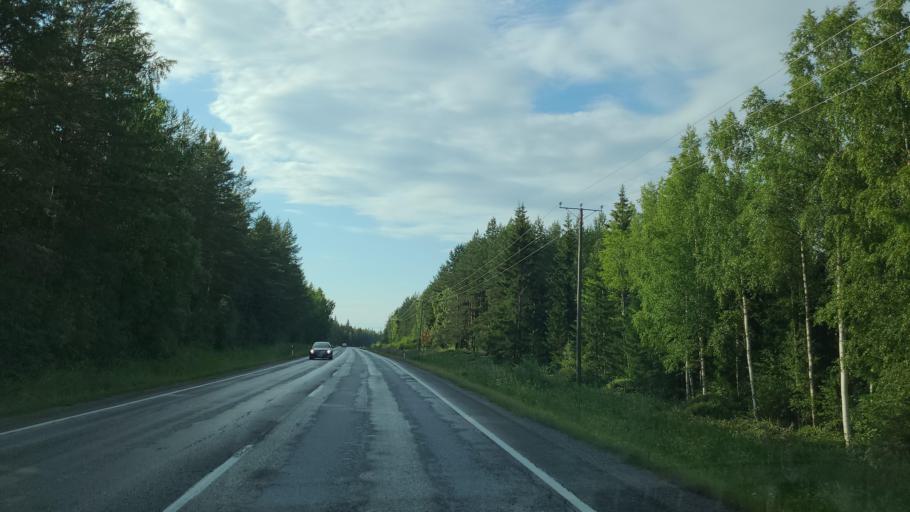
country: FI
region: Ostrobothnia
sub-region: Vaasa
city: Vaasa
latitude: 63.1801
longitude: 21.5734
